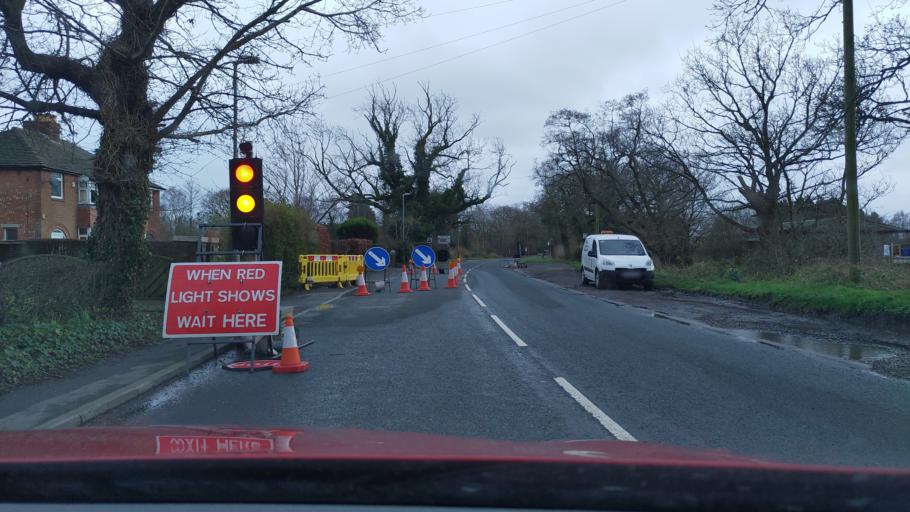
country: GB
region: England
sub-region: Lancashire
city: Croston
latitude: 53.6658
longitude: -2.7549
